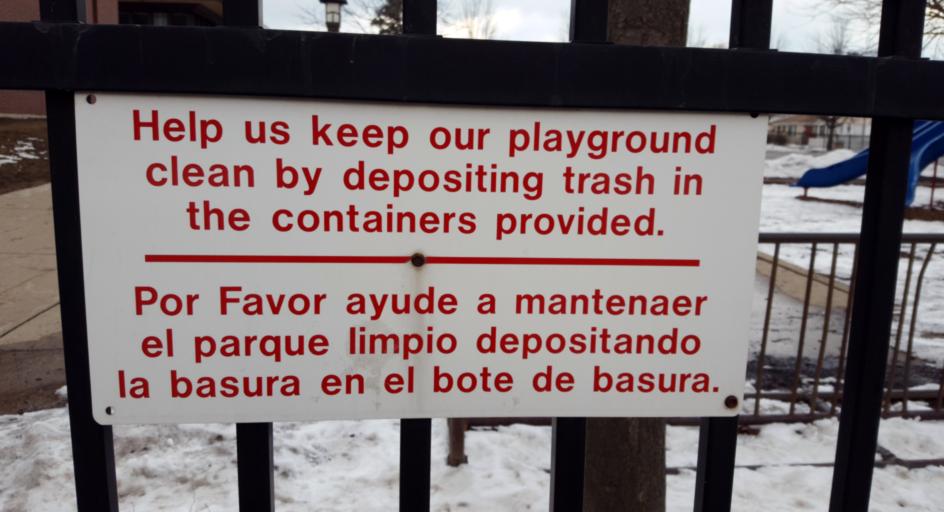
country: US
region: Illinois
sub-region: Lake County
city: Highwood
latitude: 42.1998
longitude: -87.8137
